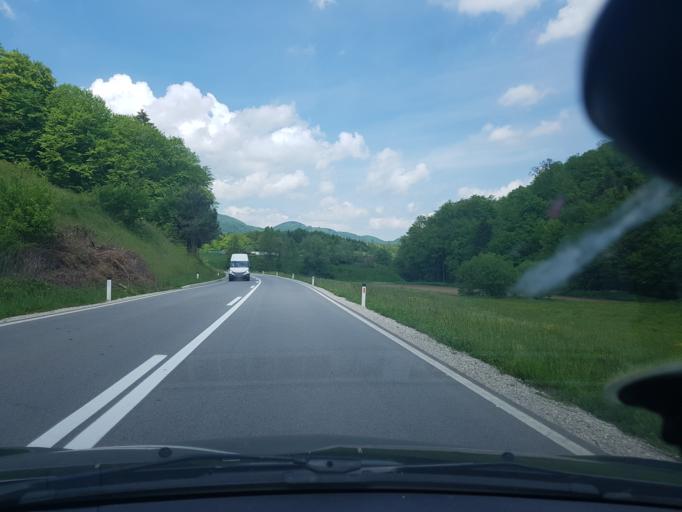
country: SI
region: Rogatec
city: Rogatec
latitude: 46.2327
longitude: 15.6730
